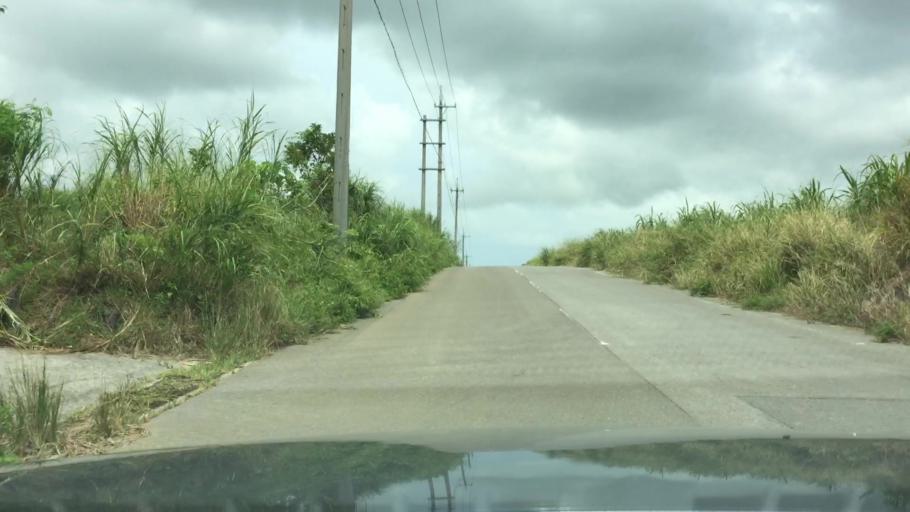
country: JP
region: Okinawa
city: Ishigaki
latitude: 24.3958
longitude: 124.1811
